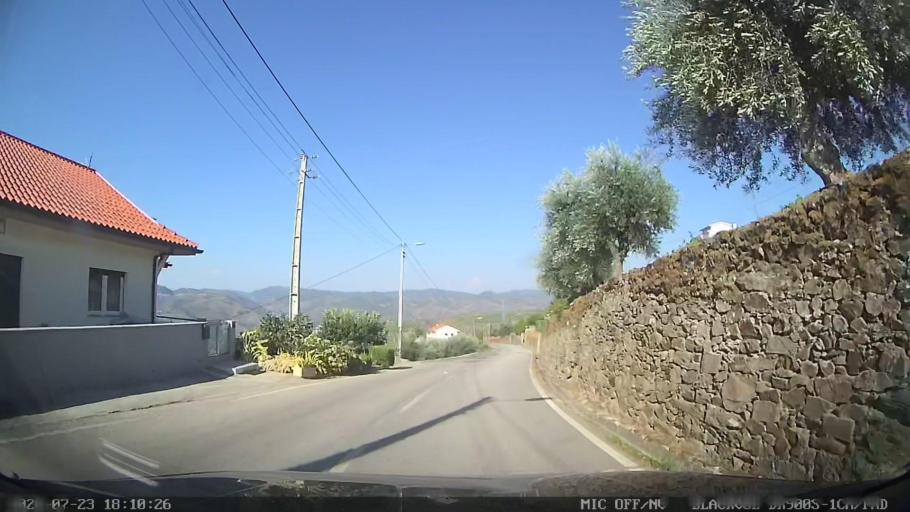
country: PT
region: Viseu
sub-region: Sao Joao da Pesqueira
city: Sao Joao da Pesqueira
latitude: 41.1881
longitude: -7.4400
